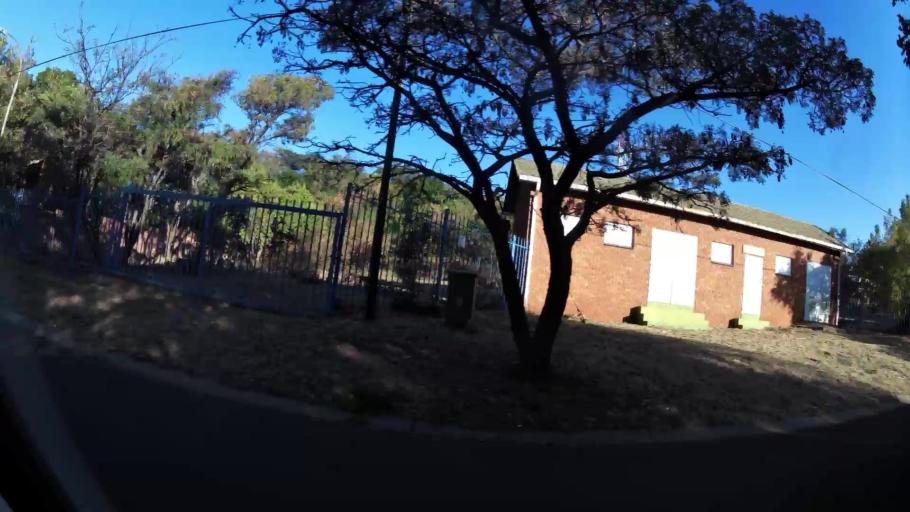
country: ZA
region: North-West
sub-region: Bojanala Platinum District Municipality
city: Rustenburg
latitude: -25.6905
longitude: 27.2075
